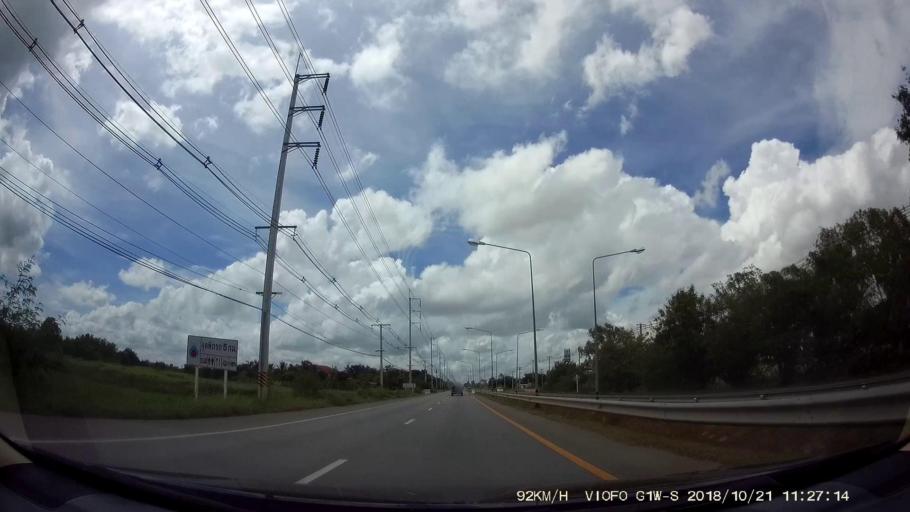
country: TH
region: Chaiyaphum
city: Chaiyaphum
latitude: 15.8016
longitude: 102.0591
